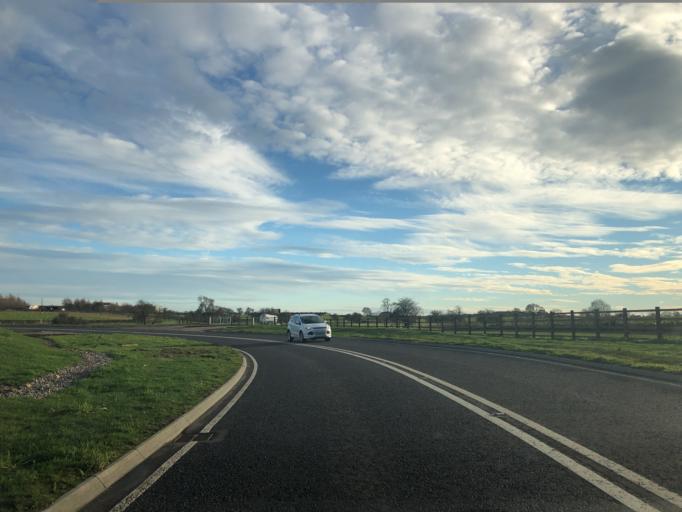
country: GB
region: England
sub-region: North Yorkshire
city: Thirsk
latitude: 54.1787
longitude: -1.3755
